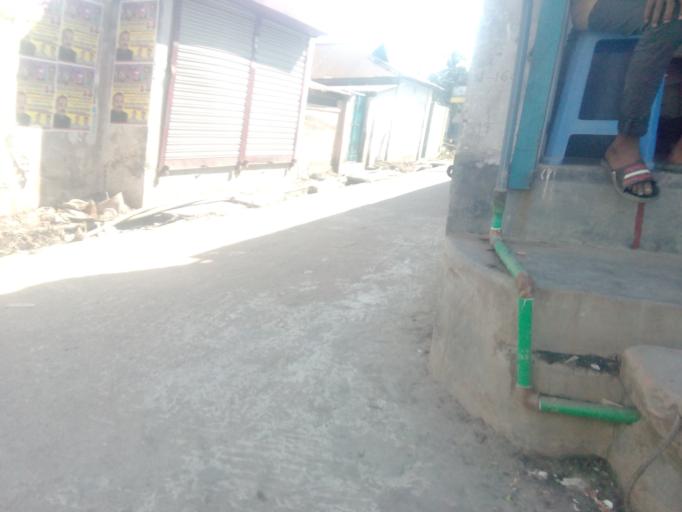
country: BD
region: Dhaka
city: Paltan
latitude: 23.7089
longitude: 90.4752
